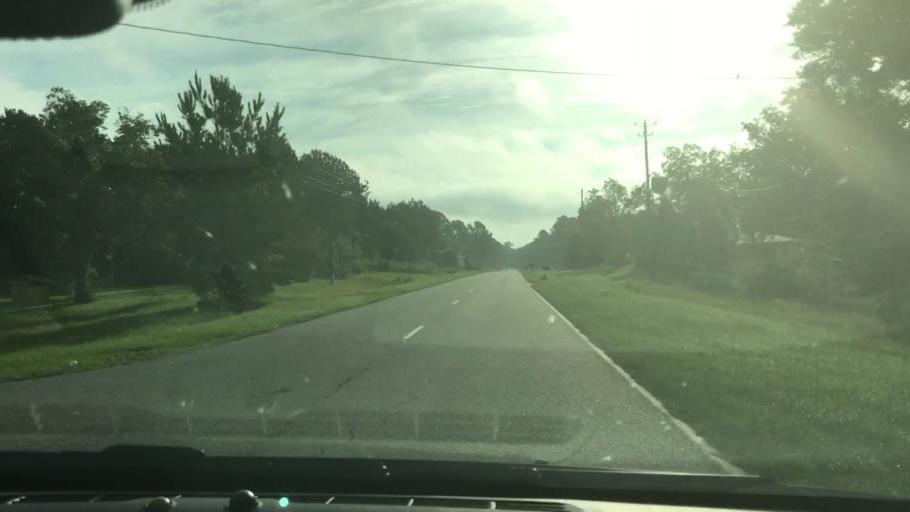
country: US
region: Georgia
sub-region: Clay County
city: Fort Gaines
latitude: 31.7195
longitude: -85.0550
